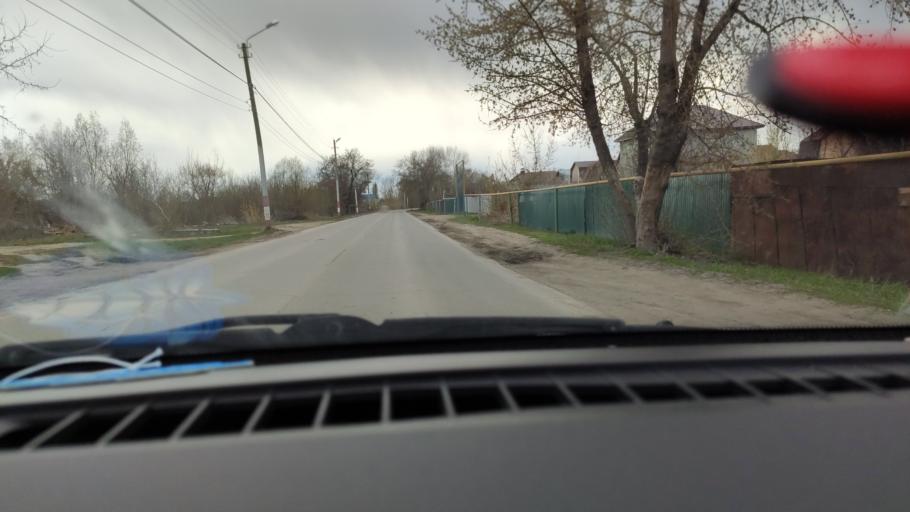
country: RU
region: Saratov
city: Engel's
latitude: 51.4938
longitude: 46.0549
